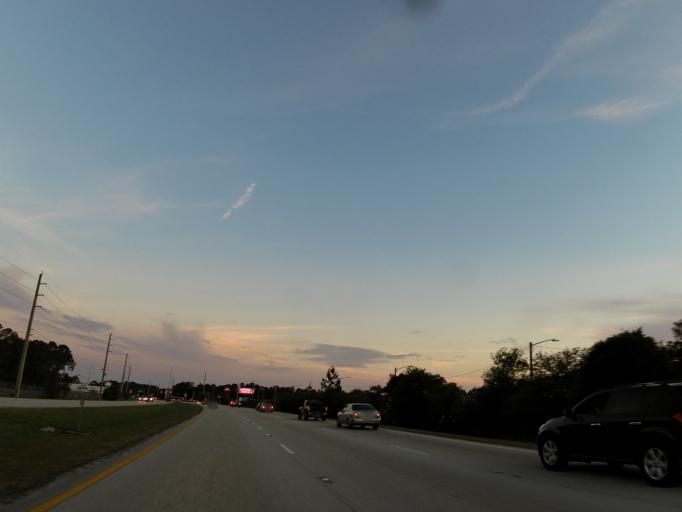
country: US
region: Florida
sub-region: Clay County
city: Orange Park
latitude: 30.1999
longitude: -81.7073
